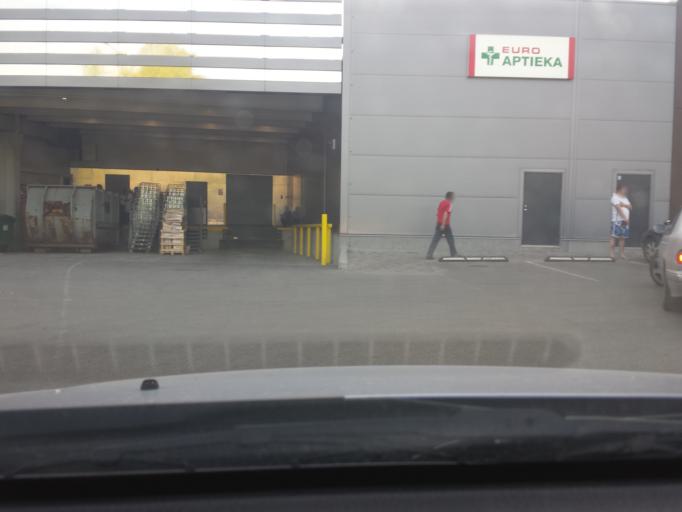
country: LV
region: Riga
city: Riga
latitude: 56.9637
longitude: 24.1670
